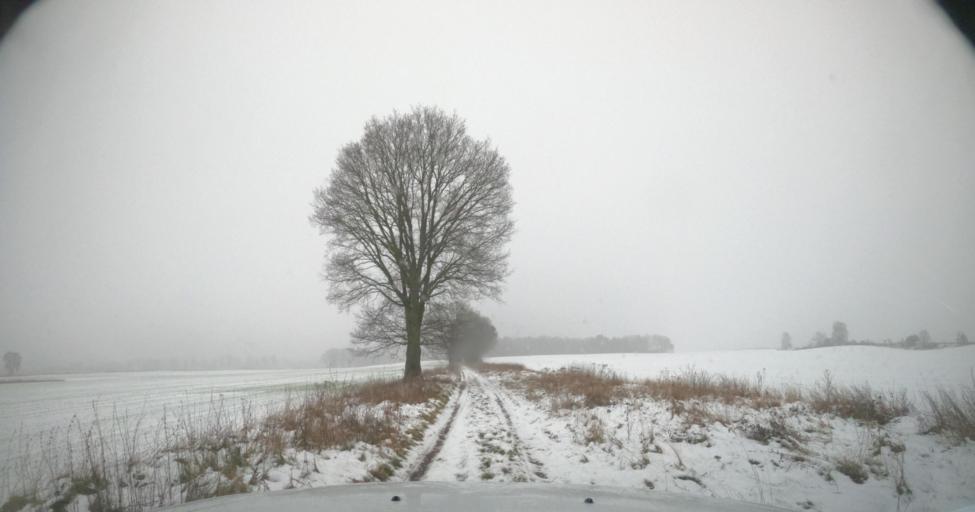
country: PL
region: West Pomeranian Voivodeship
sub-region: Powiat kamienski
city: Golczewo
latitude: 53.8631
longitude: 15.0258
